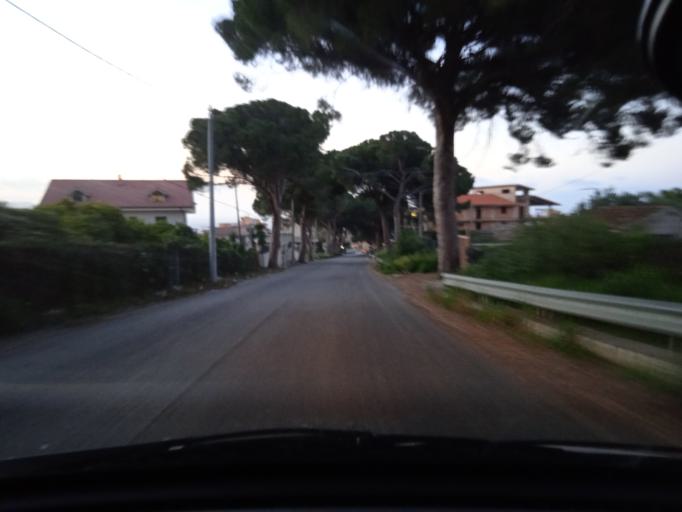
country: IT
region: Sicily
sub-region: Palermo
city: Portella di Mare
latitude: 38.0662
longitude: 13.4589
